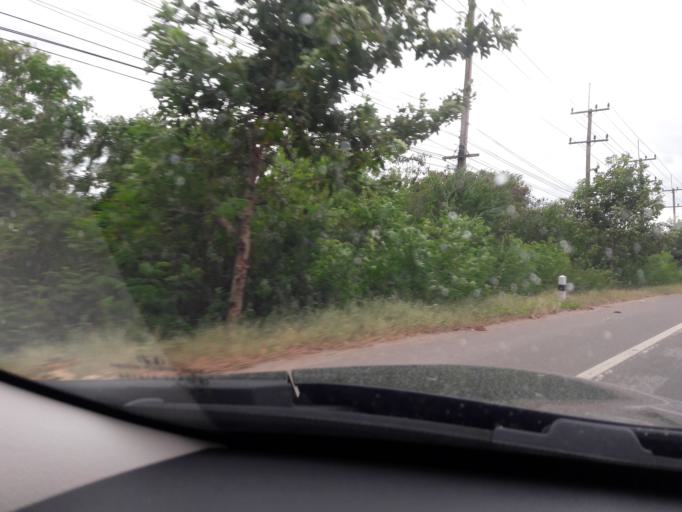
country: TH
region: Ratchaburi
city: Bang Phae
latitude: 13.6382
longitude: 99.9489
